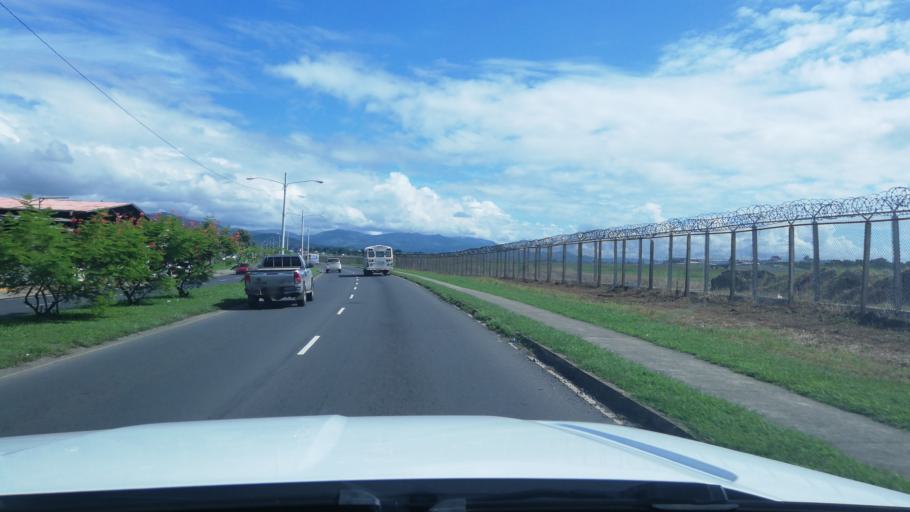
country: PA
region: Panama
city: Tocumen
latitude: 9.0783
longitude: -79.3859
